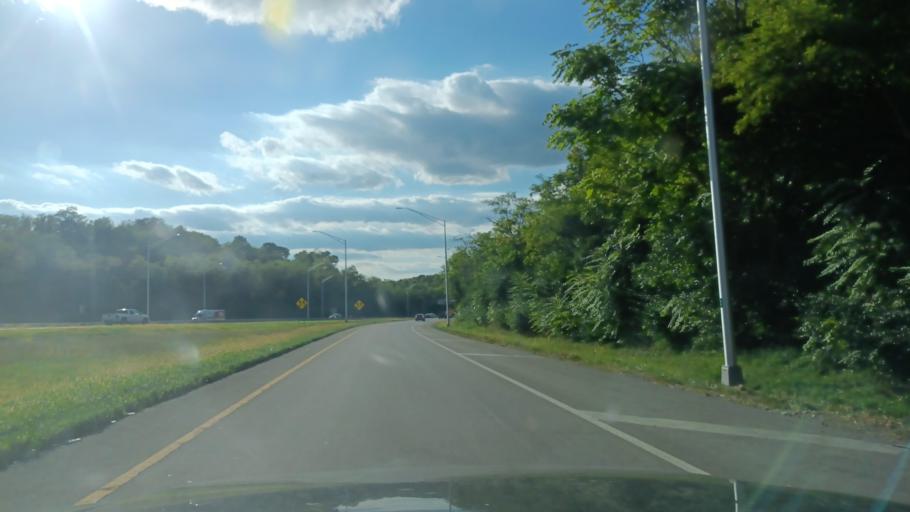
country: US
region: Ohio
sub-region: Greene County
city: Xenia
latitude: 39.6941
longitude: -83.9782
